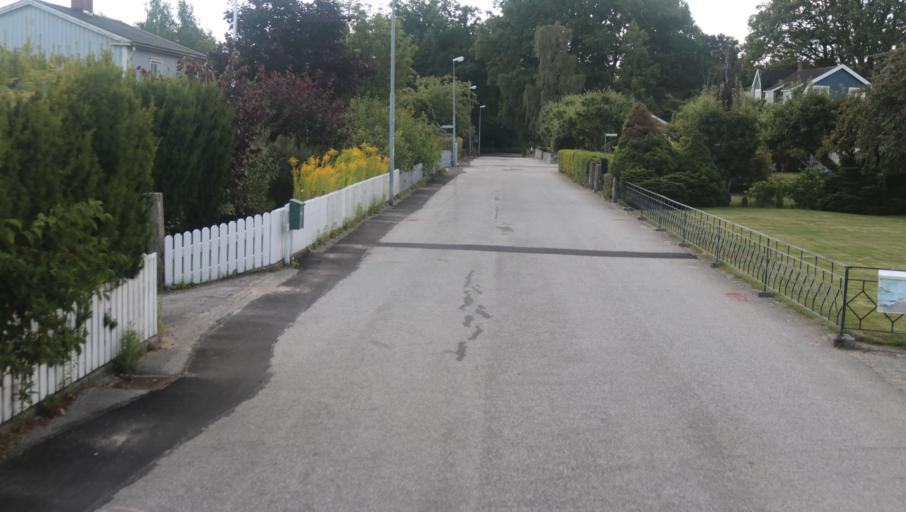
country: SE
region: Blekinge
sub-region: Karlshamns Kommun
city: Morrum
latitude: 56.1905
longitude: 14.7480
